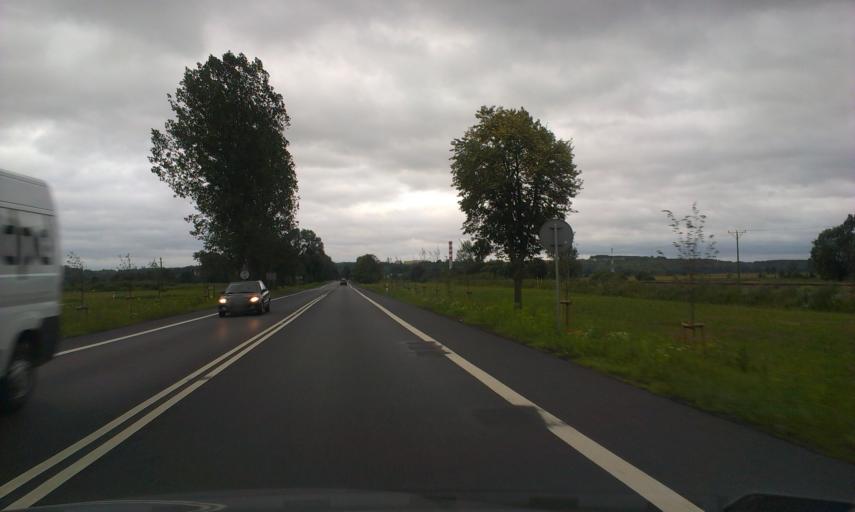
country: PL
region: Greater Poland Voivodeship
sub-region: Powiat pilski
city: Ujscie
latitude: 53.0712
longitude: 16.7315
